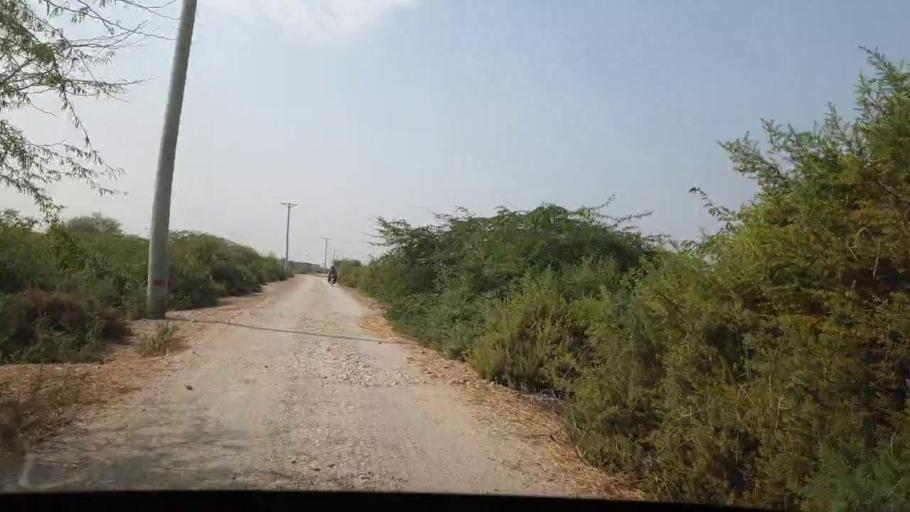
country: PK
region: Sindh
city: Chuhar Jamali
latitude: 24.2721
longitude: 67.9008
